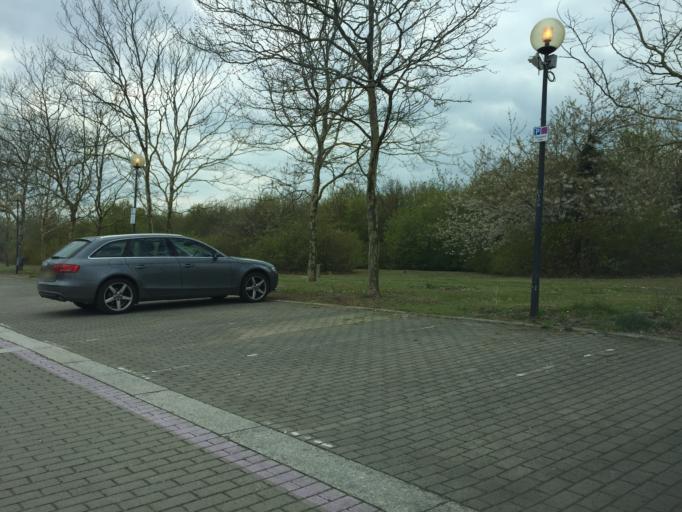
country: GB
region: England
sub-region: Milton Keynes
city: Milton Keynes
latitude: 52.0435
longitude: -0.7637
